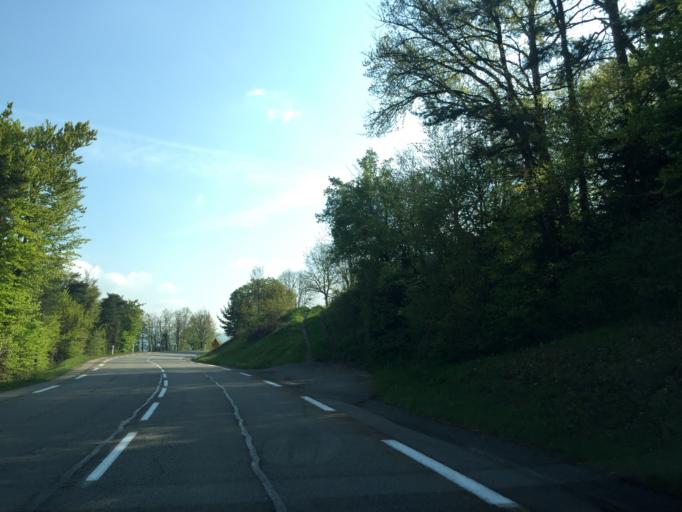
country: FR
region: Rhone-Alpes
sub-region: Departement de l'Isere
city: Mens
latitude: 44.7797
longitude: 5.6474
